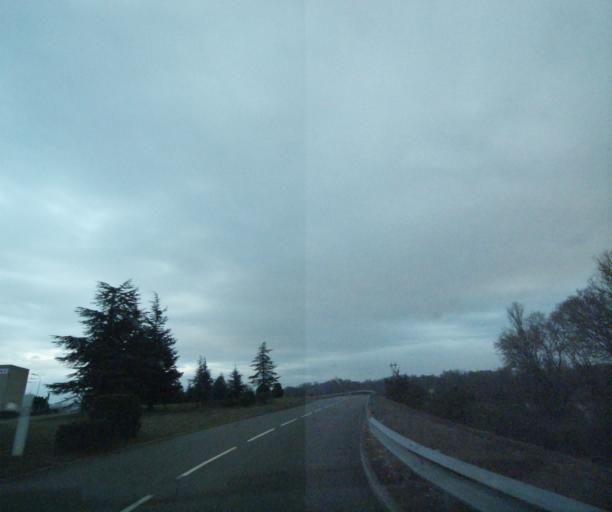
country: FR
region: Rhone-Alpes
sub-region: Departement de l'Ardeche
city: Cornas
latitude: 44.9614
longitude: 4.8695
